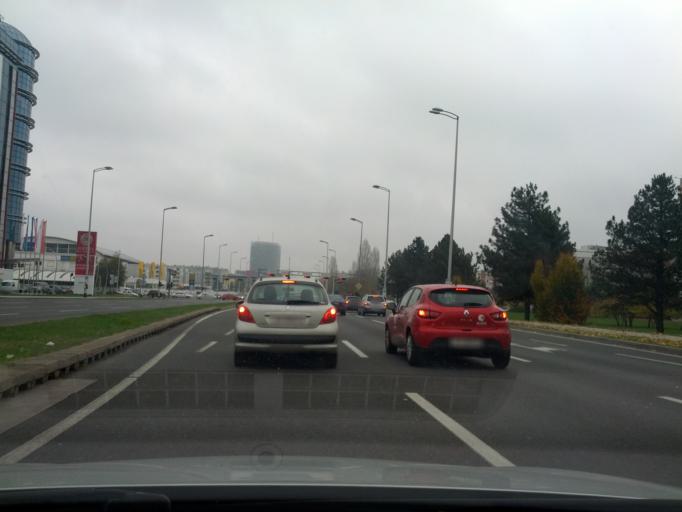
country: HR
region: Grad Zagreb
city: Jankomir
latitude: 45.7969
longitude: 15.8977
